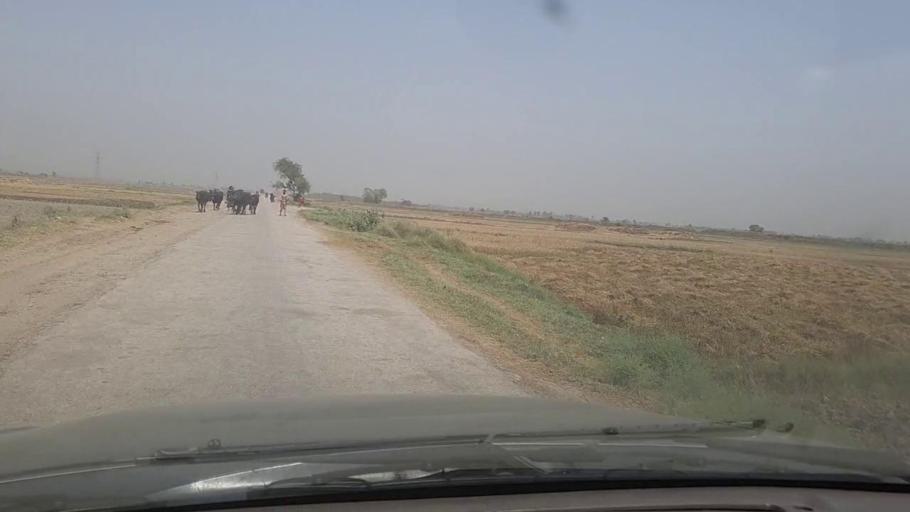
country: PK
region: Sindh
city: Madeji
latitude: 27.8053
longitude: 68.4004
